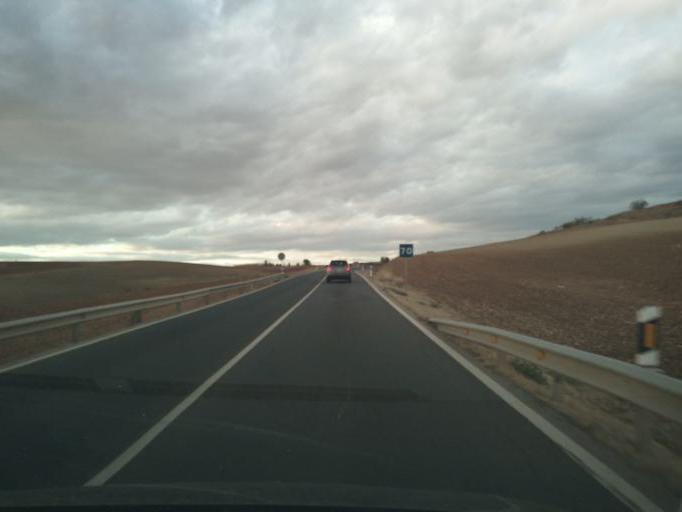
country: ES
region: Madrid
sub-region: Provincia de Madrid
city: Ajalvir
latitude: 40.5232
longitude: -3.4947
